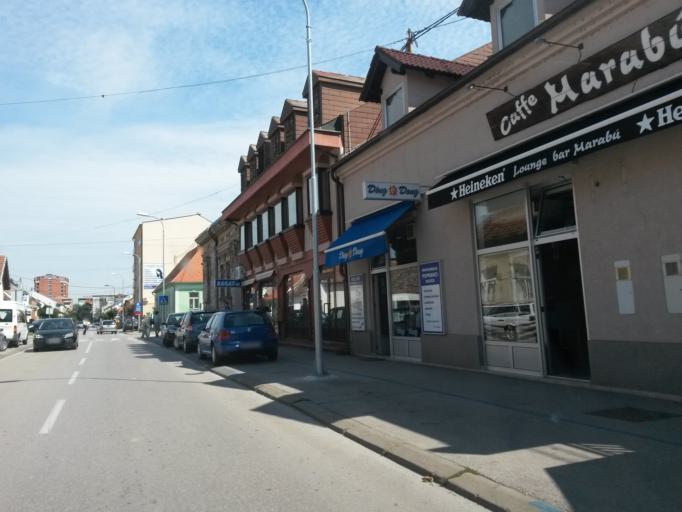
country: HR
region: Vukovarsko-Srijemska
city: Vinkovci
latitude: 45.2890
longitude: 18.8022
